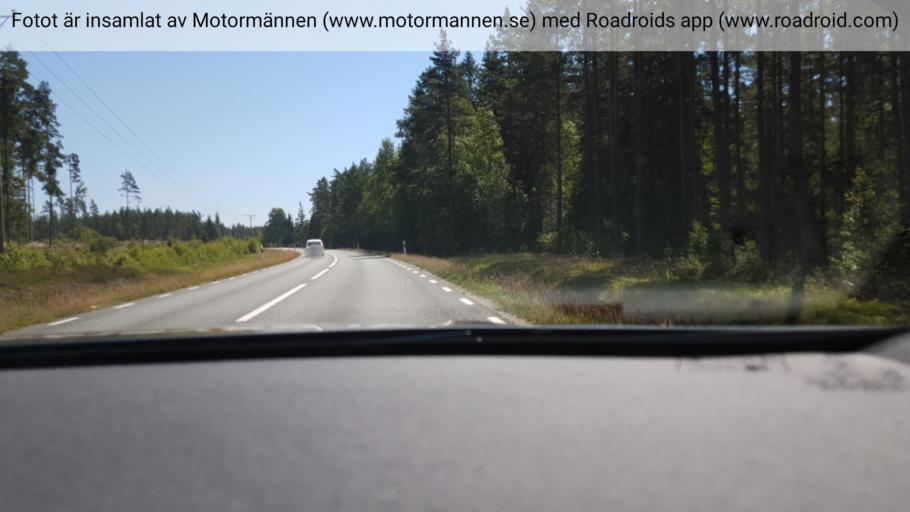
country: SE
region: Joenkoeping
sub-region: Gnosjo Kommun
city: Gnosjoe
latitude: 57.3860
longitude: 13.6975
